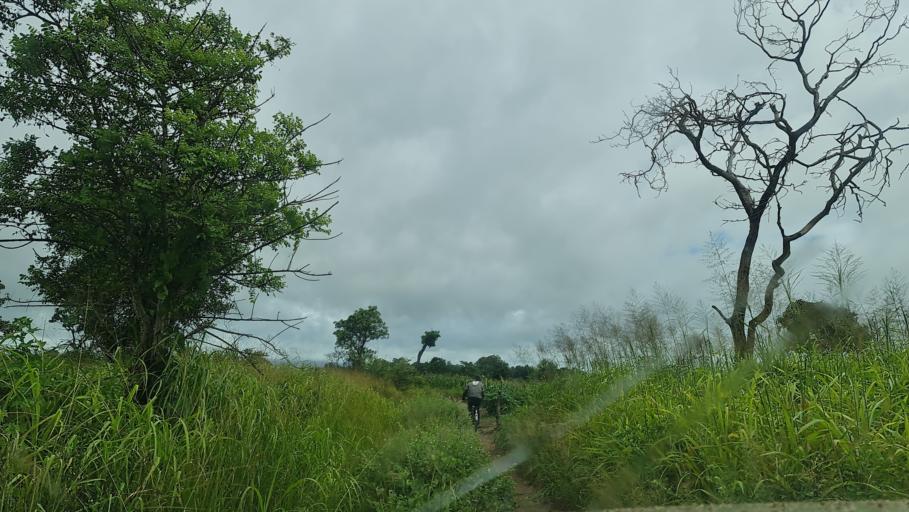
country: MW
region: Southern Region
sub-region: Nsanje District
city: Nsanje
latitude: -17.4434
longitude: 35.8455
